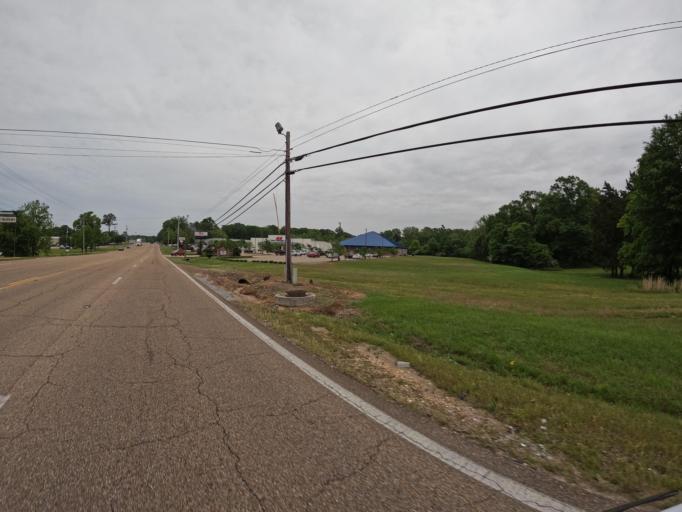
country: US
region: Mississippi
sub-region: Lee County
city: Tupelo
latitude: 34.2865
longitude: -88.7407
